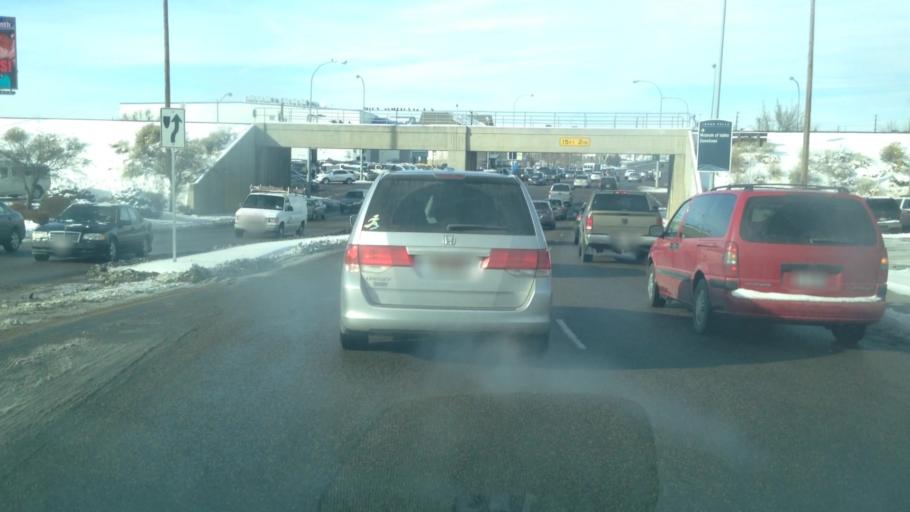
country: US
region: Idaho
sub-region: Bonneville County
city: Idaho Falls
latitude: 43.4829
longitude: -112.0438
